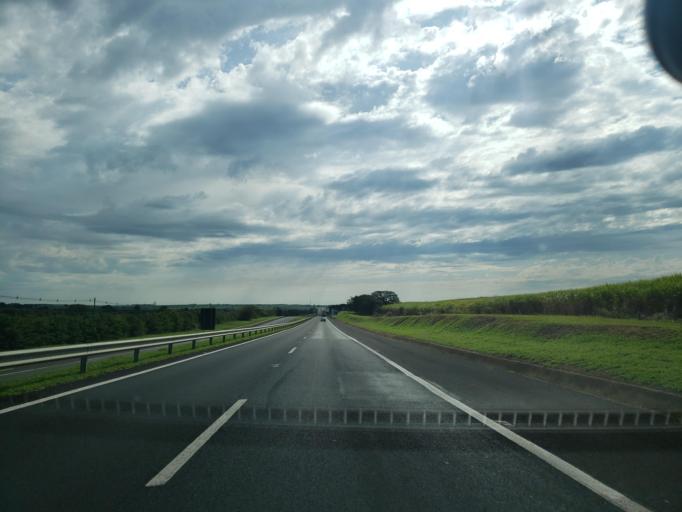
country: BR
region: Sao Paulo
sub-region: Cafelandia
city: Cafelandia
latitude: -21.8703
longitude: -49.5670
